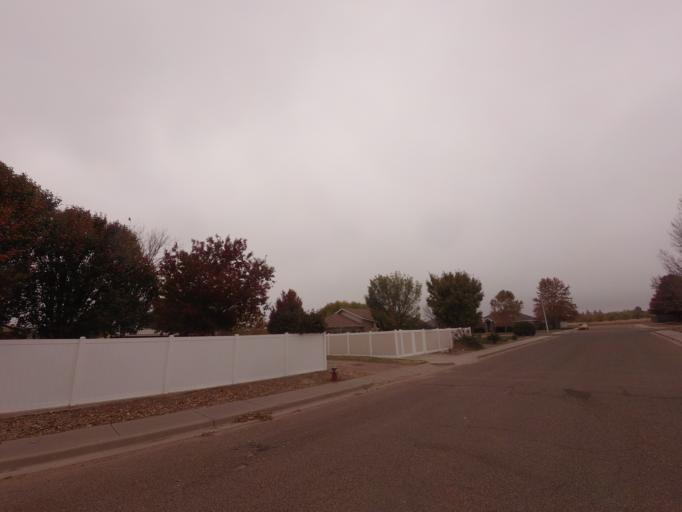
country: US
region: New Mexico
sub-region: Curry County
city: Clovis
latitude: 34.4274
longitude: -103.1854
